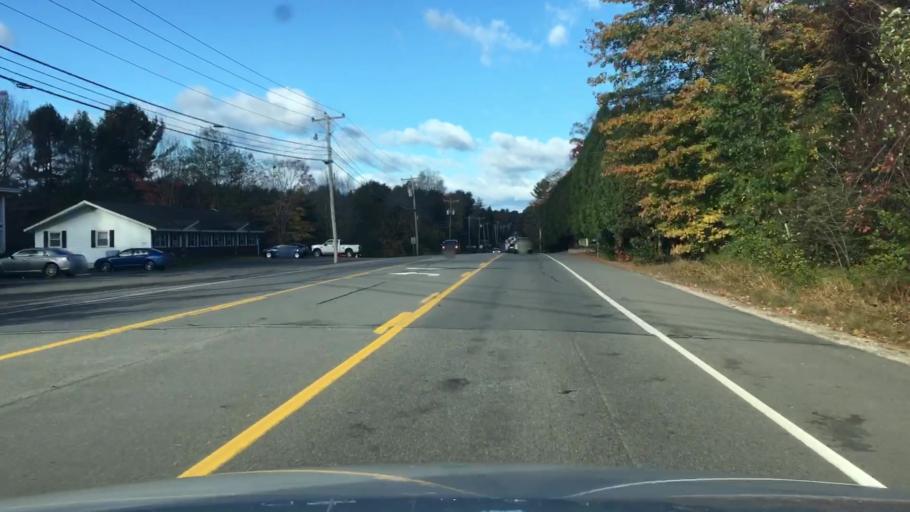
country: US
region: New Hampshire
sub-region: Strafford County
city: Lee
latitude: 43.1496
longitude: -71.0103
